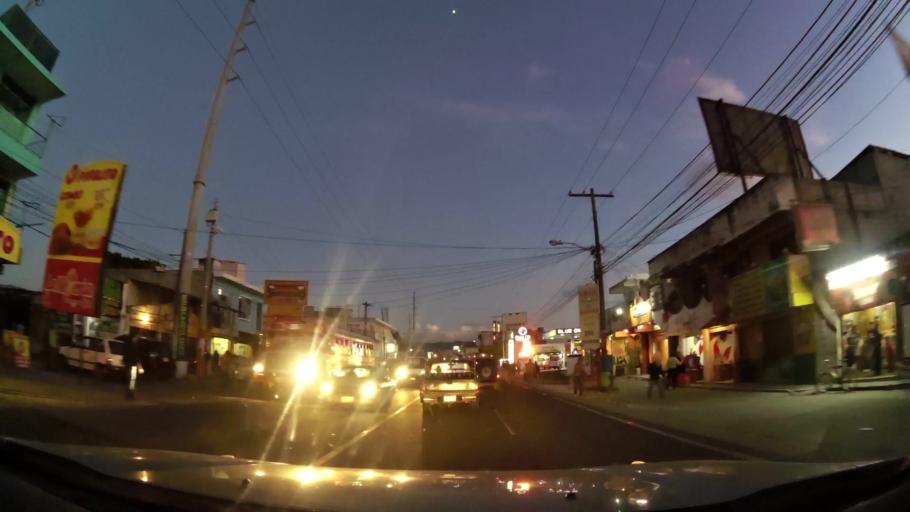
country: GT
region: Guatemala
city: Petapa
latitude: 14.5042
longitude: -90.5658
